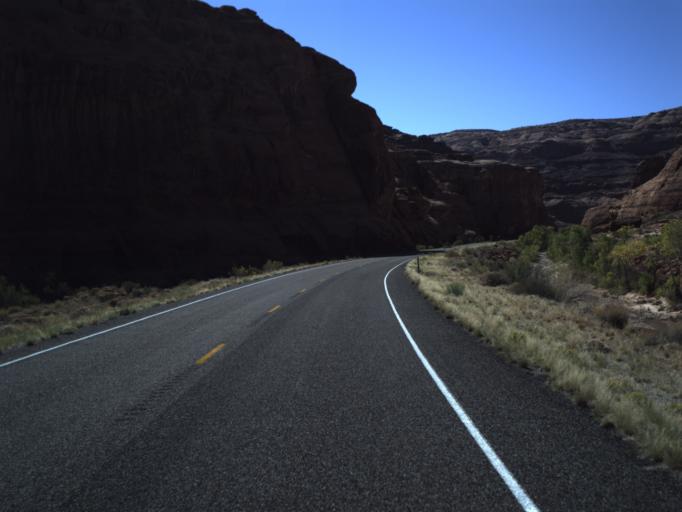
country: US
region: Utah
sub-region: San Juan County
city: Blanding
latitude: 37.9764
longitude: -110.4916
